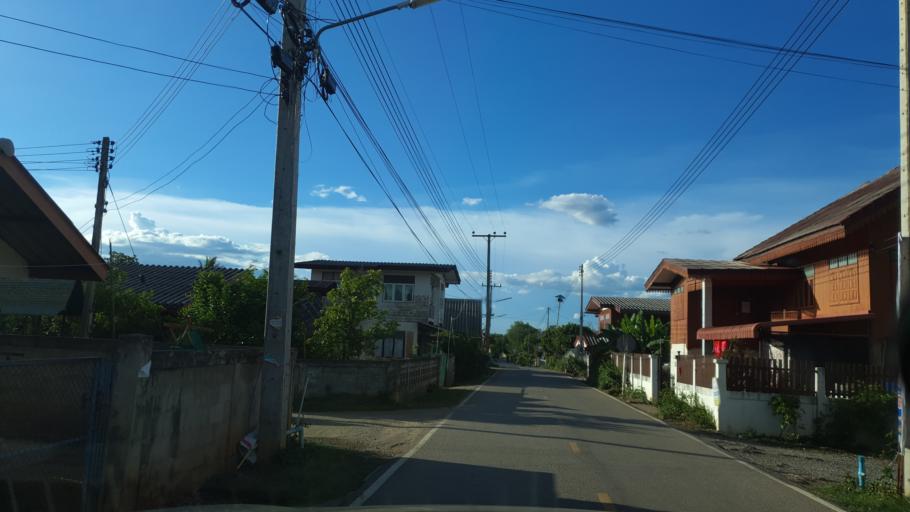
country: TH
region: Lampang
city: Sop Prap
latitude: 17.8850
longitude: 99.3115
